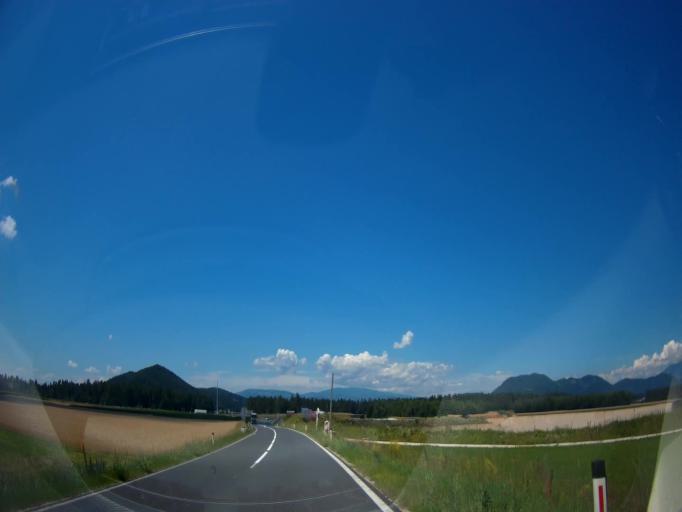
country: AT
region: Carinthia
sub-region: Politischer Bezirk Volkermarkt
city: Bleiburg/Pliberk
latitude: 46.6056
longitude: 14.7852
